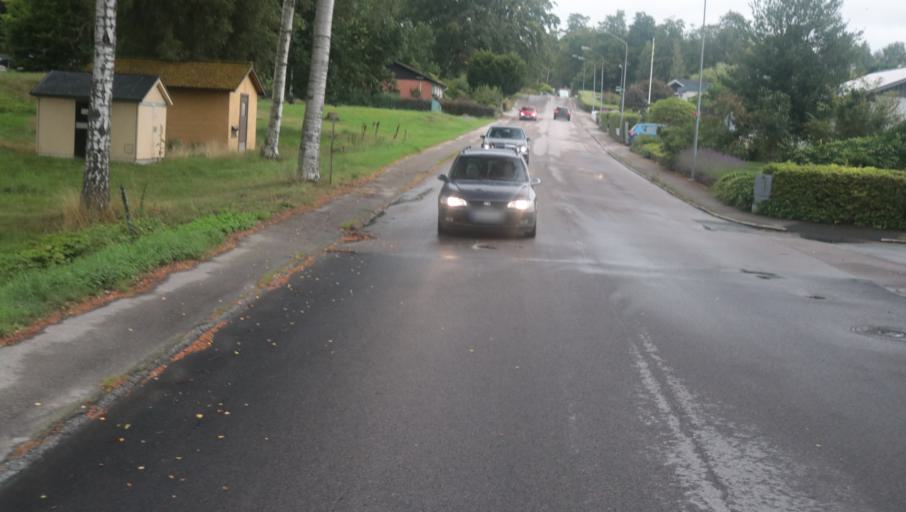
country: SE
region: Blekinge
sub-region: Karlshamns Kommun
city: Svangsta
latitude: 56.2580
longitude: 14.7784
